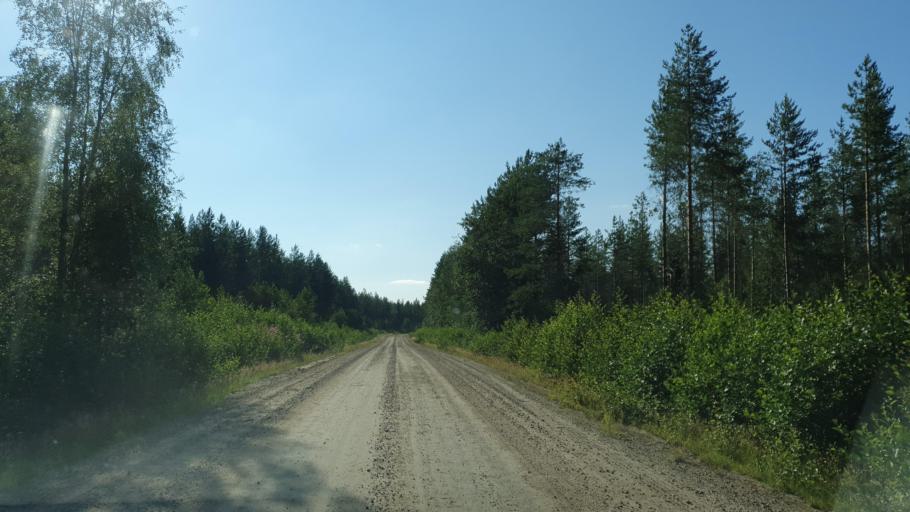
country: FI
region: Kainuu
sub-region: Kehys-Kainuu
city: Kuhmo
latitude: 64.0282
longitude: 29.7051
